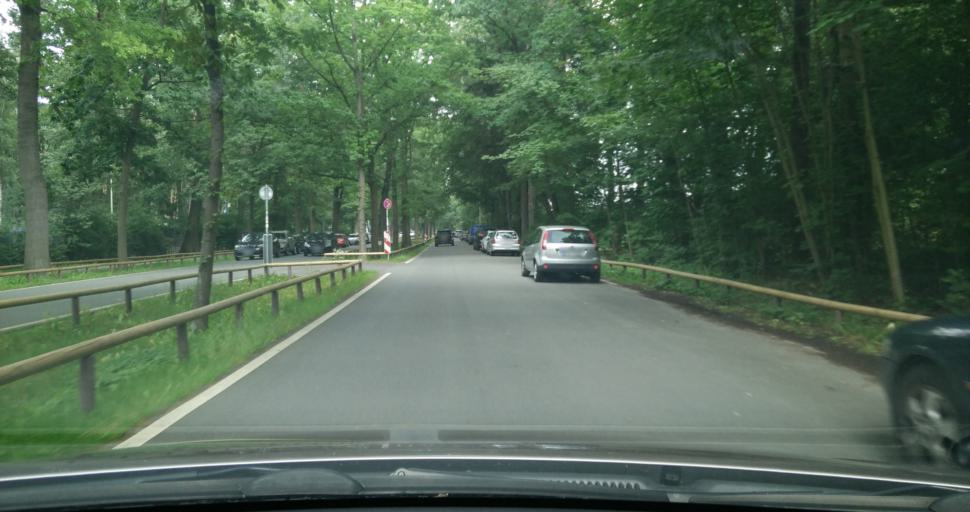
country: DE
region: Bavaria
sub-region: Regierungsbezirk Mittelfranken
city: Nuernberg
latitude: 49.4228
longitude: 11.1248
